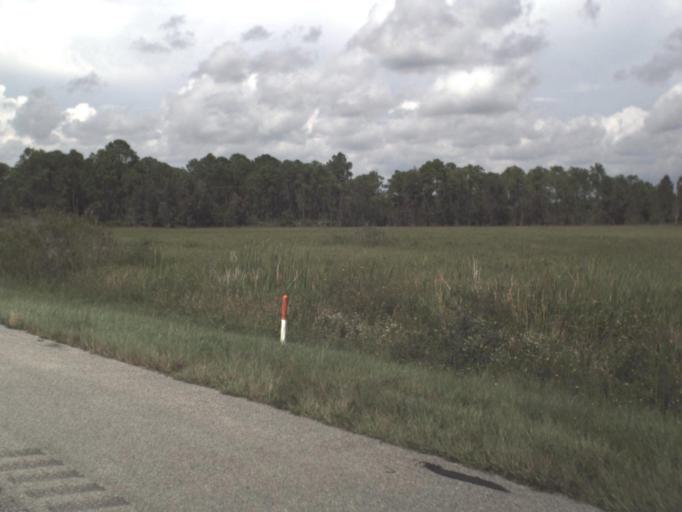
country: US
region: Florida
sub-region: Lee County
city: Suncoast Estates
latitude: 26.8060
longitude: -81.9253
